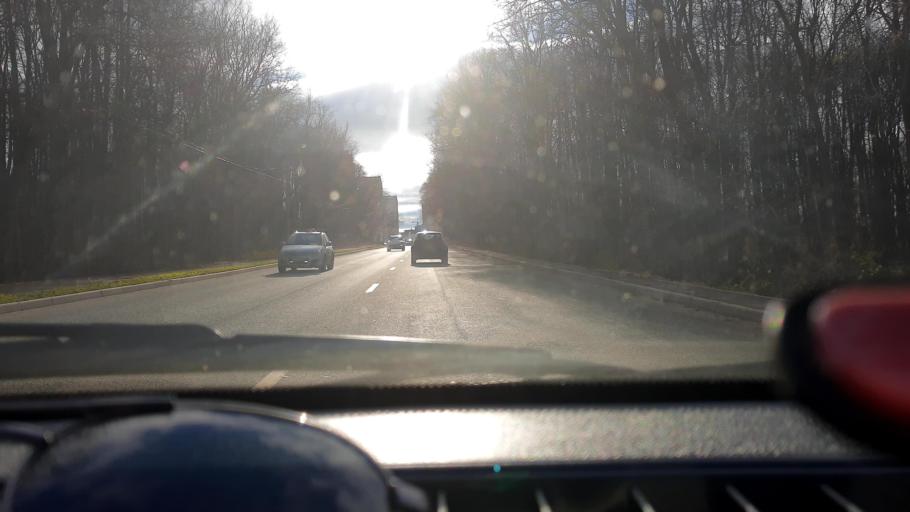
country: RU
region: Bashkortostan
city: Ufa
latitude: 54.7830
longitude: 56.0263
